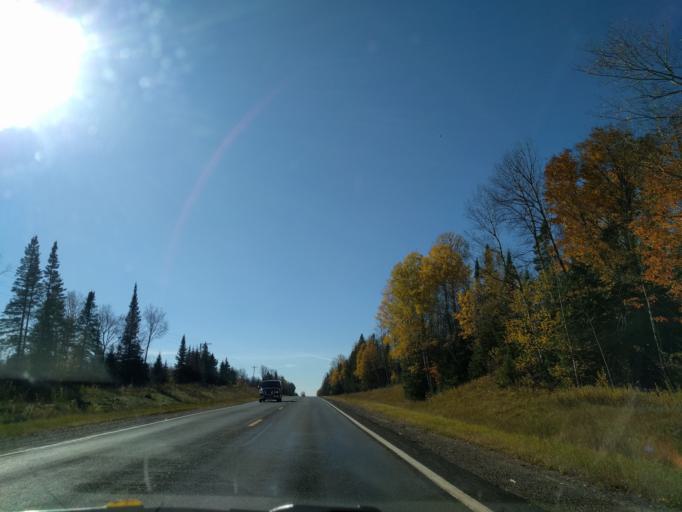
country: US
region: Michigan
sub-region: Marquette County
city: West Ishpeming
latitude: 46.3068
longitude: -87.9852
